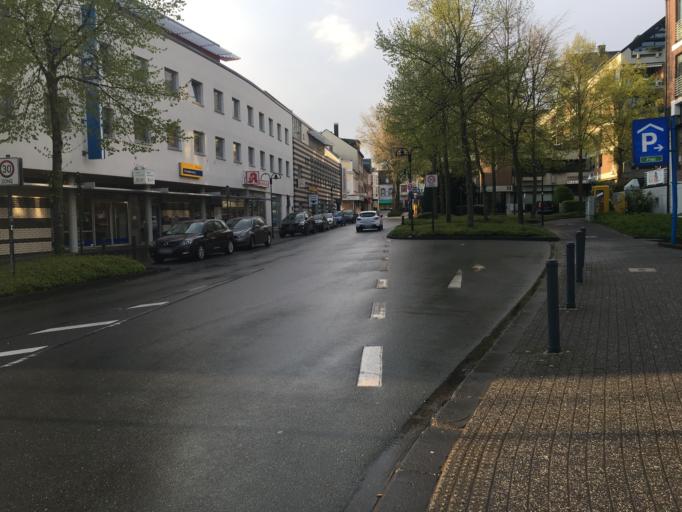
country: DE
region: North Rhine-Westphalia
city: Haan
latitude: 51.1599
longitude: 7.0000
